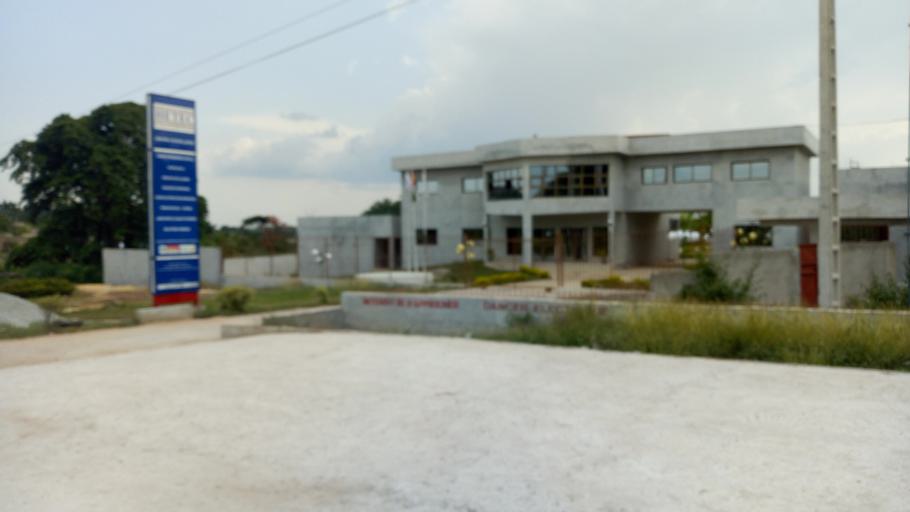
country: CI
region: Vallee du Bandama
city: Bouake
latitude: 7.6642
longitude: -5.0276
